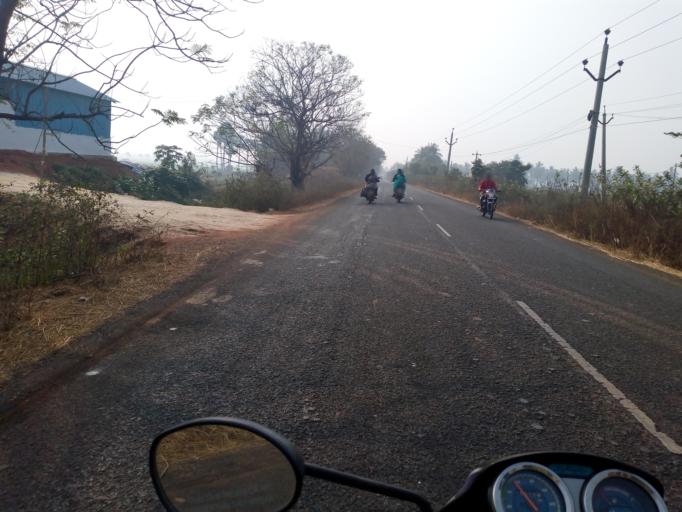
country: IN
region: Andhra Pradesh
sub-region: West Godavari
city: Tadepallegudem
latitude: 16.7893
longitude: 81.4191
